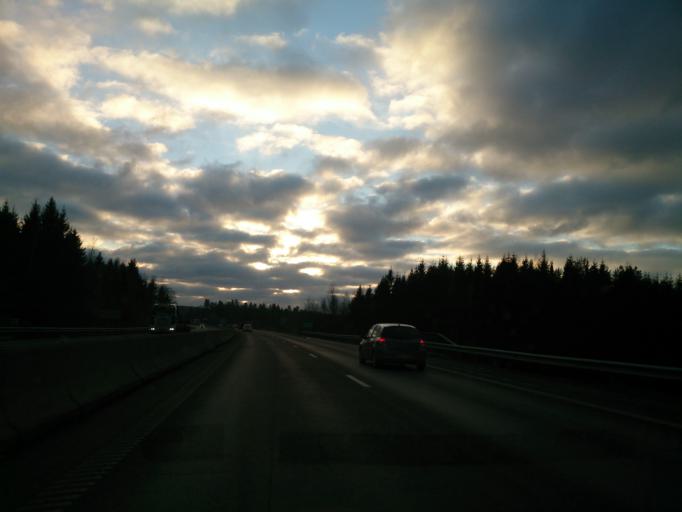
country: SE
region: OEstergoetland
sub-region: Norrkopings Kommun
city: Kimstad
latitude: 58.5622
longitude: 16.0638
